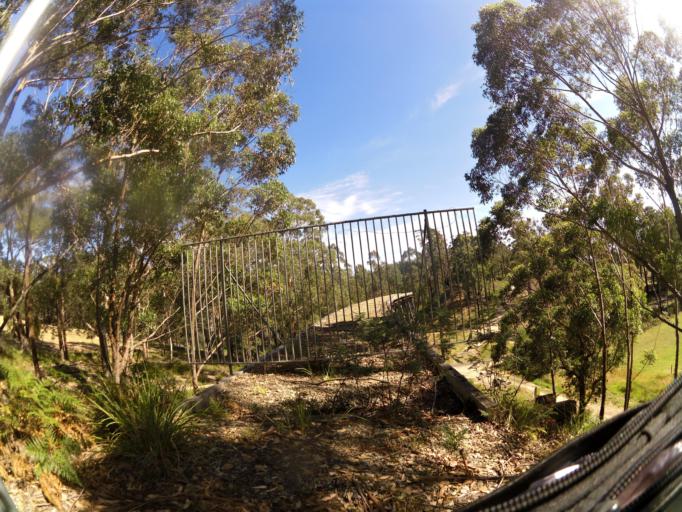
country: AU
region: Victoria
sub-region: East Gippsland
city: Lakes Entrance
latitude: -37.7329
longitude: 148.1621
